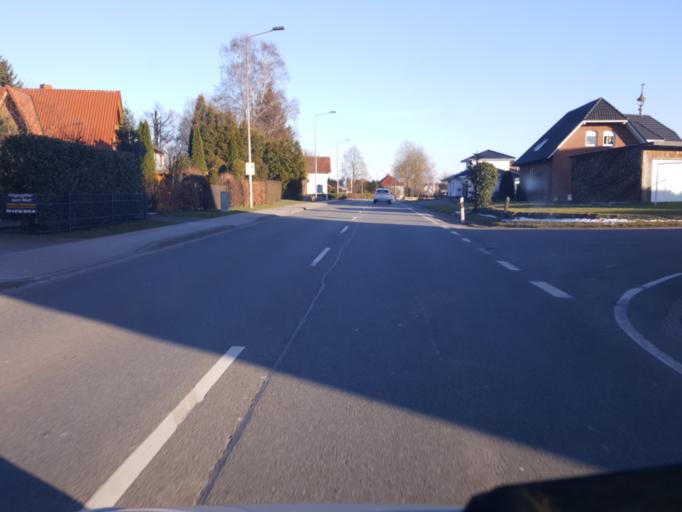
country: DE
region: North Rhine-Westphalia
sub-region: Regierungsbezirk Detmold
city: Hille
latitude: 52.3406
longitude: 8.7382
